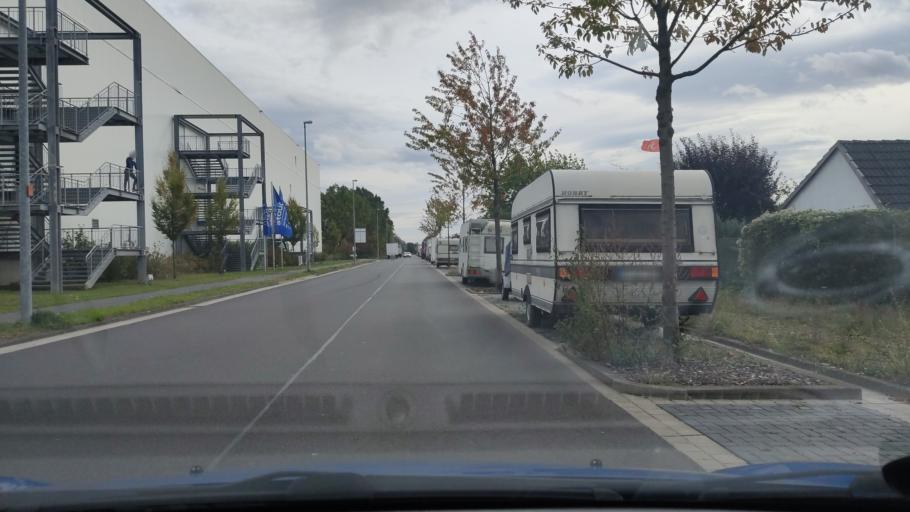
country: DE
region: Lower Saxony
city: Hannover
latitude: 52.4064
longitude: 9.7034
